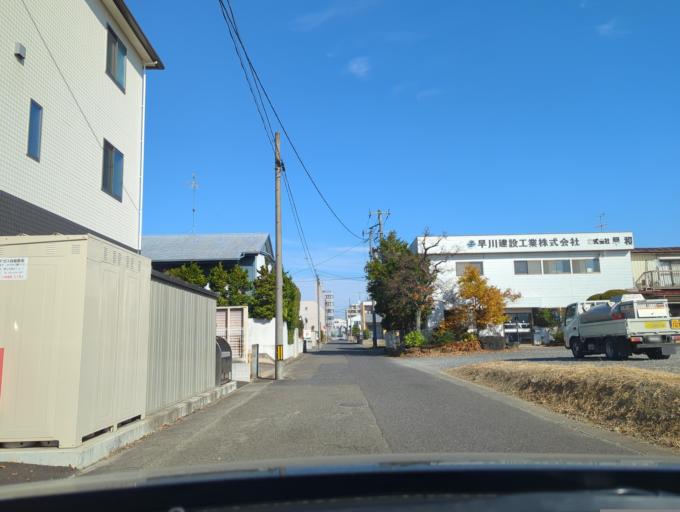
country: JP
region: Fukushima
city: Koriyama
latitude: 37.3565
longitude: 140.3628
